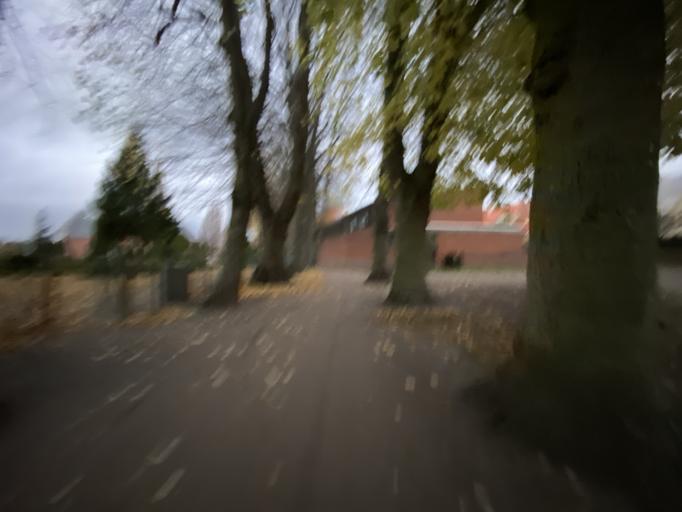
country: DK
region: Capital Region
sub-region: Dragor Kommune
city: Dragor
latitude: 55.5930
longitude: 12.6687
